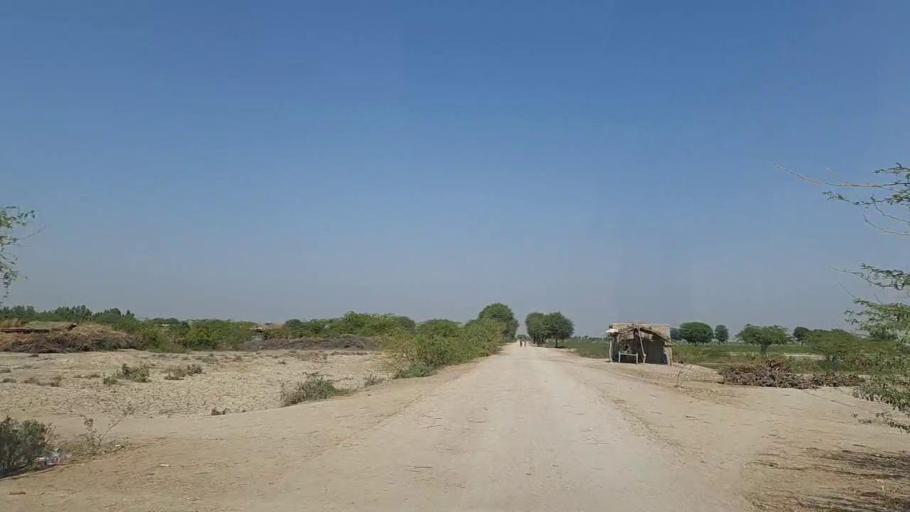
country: PK
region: Sindh
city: Samaro
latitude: 25.1875
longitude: 69.4041
